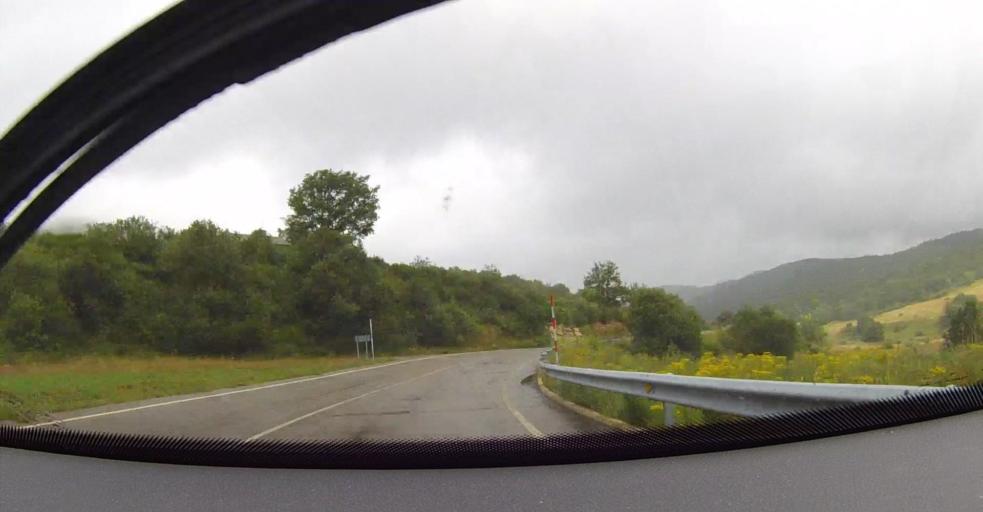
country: ES
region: Castille and Leon
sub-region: Provincia de Leon
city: Marana
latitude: 43.0726
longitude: -5.1963
